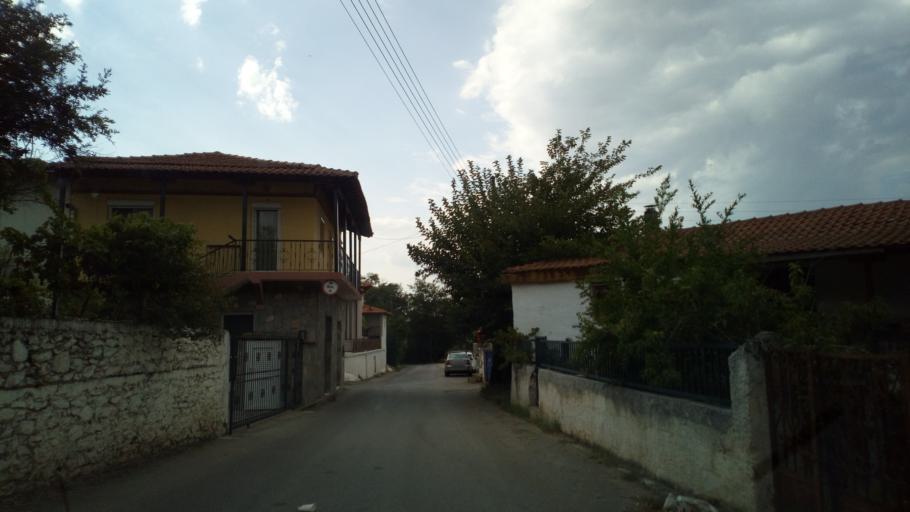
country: GR
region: Central Macedonia
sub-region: Nomos Chalkidikis
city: Galatista
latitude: 40.5133
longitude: 23.3499
